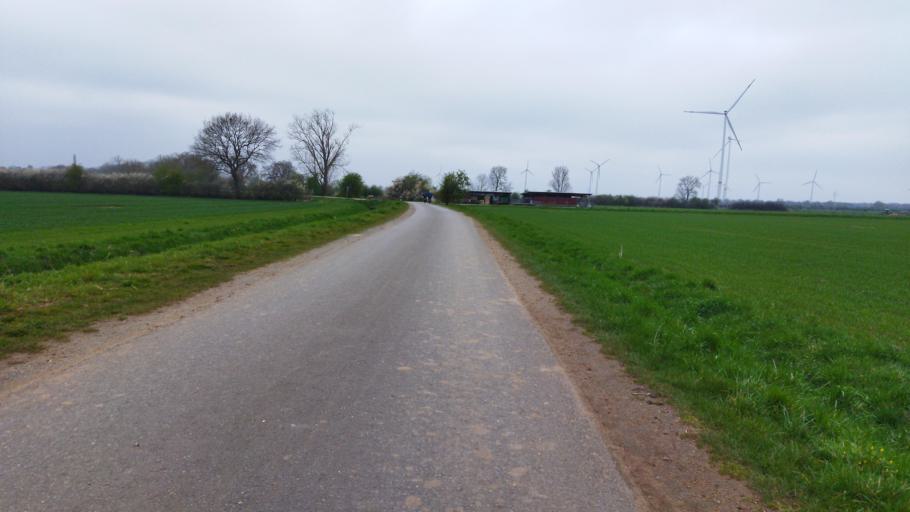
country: DE
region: Lower Saxony
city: Riede
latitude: 53.0103
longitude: 8.9619
